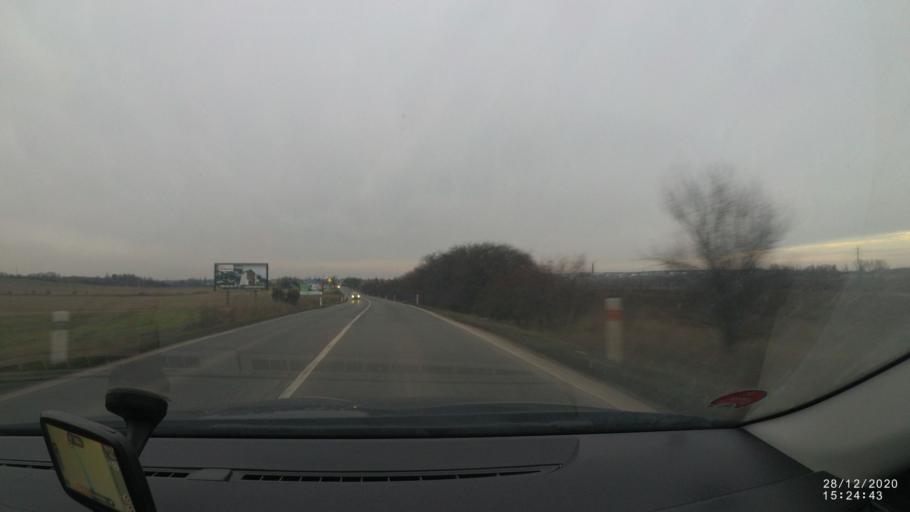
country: CZ
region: Praha
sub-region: Praha 20
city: Horni Pocernice
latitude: 50.0800
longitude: 14.6352
